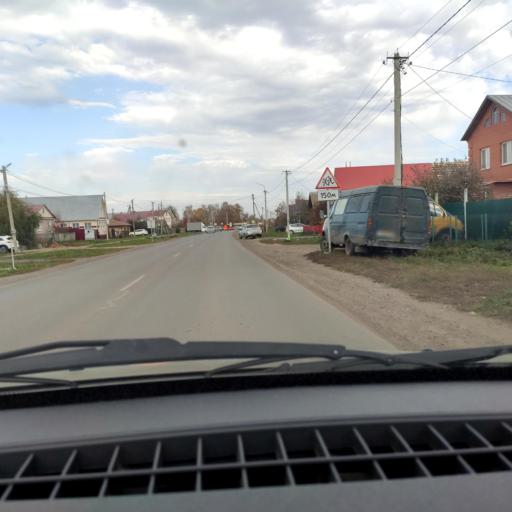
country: RU
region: Bashkortostan
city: Ufa
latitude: 54.6128
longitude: 55.9011
